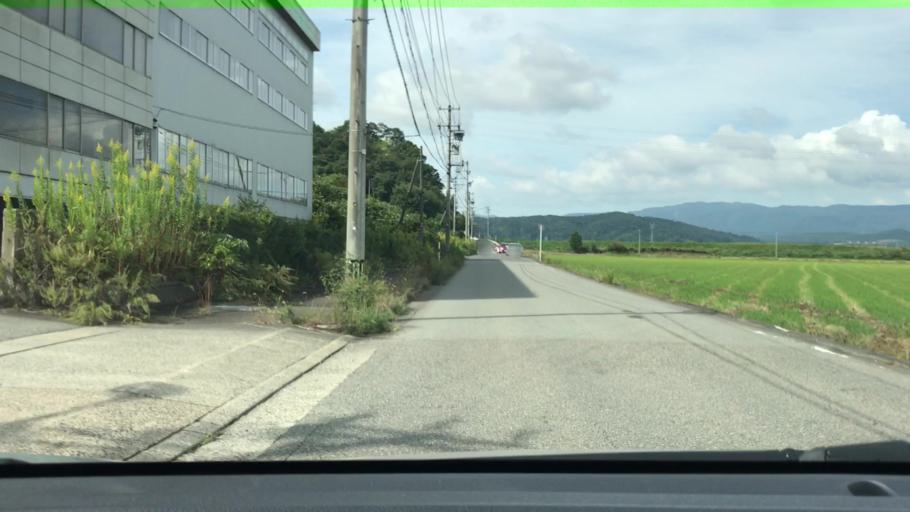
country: JP
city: Asahi
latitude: 36.0138
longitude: 136.1705
